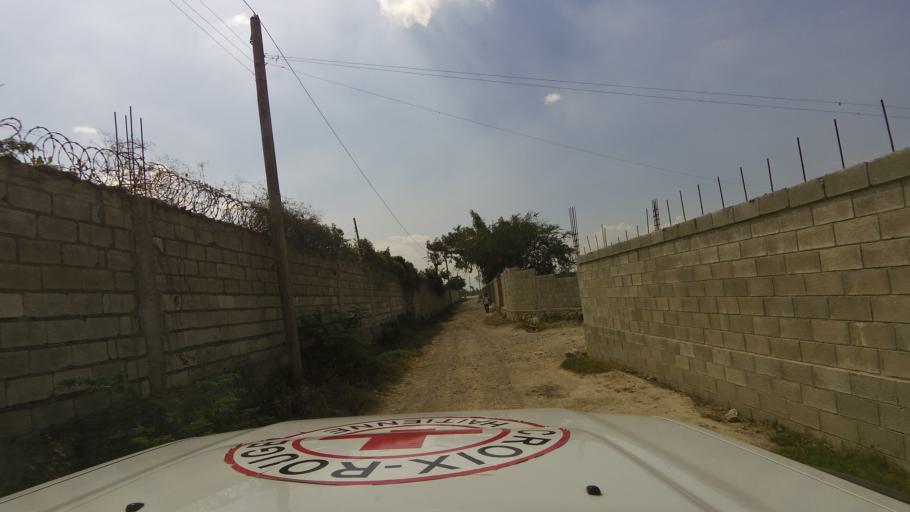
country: HT
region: Ouest
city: Croix des Bouquets
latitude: 18.6423
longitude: -72.2707
